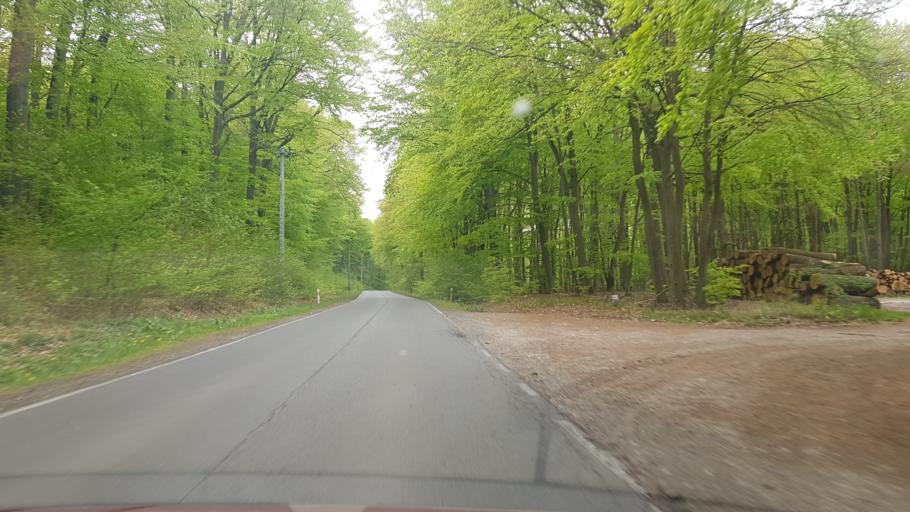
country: PL
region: West Pomeranian Voivodeship
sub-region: Powiat gryfinski
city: Stare Czarnowo
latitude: 53.2849
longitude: 14.7494
